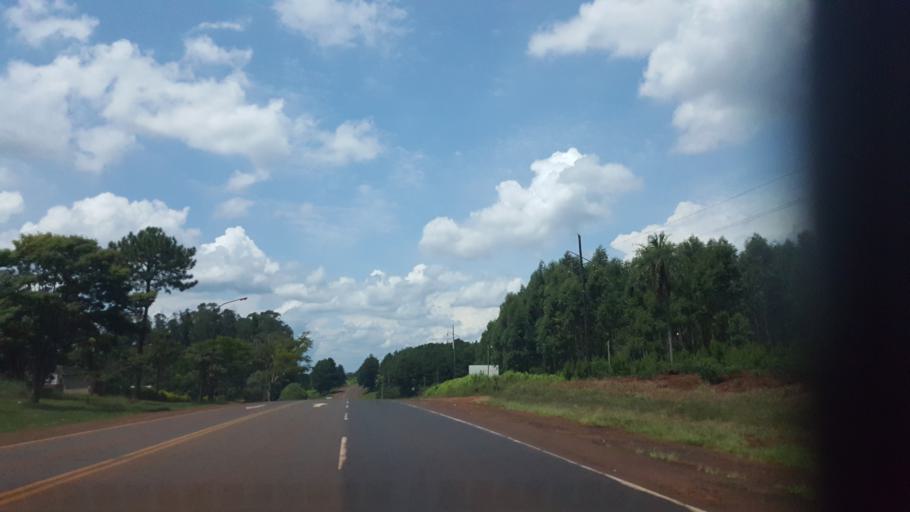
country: AR
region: Misiones
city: Garuhape
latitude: -26.8206
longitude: -54.9912
